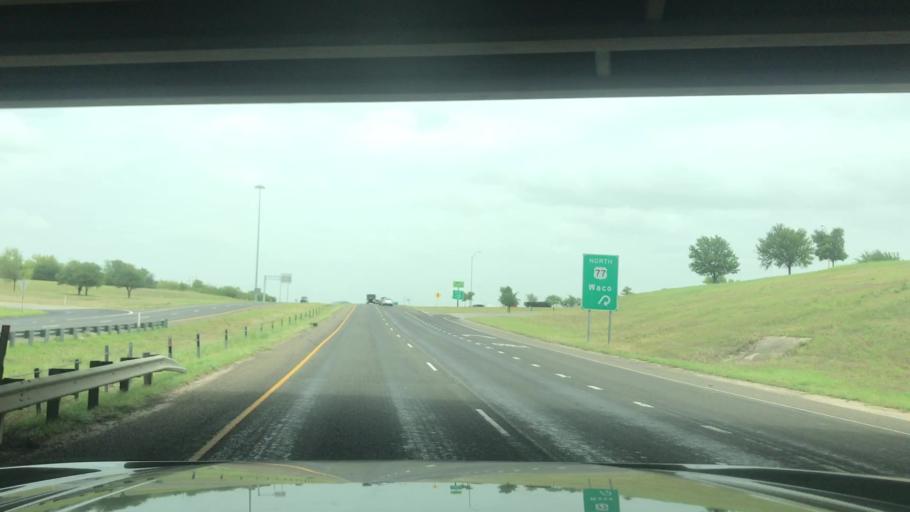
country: US
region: Texas
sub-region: McLennan County
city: Beverly
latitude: 31.4986
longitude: -97.1249
